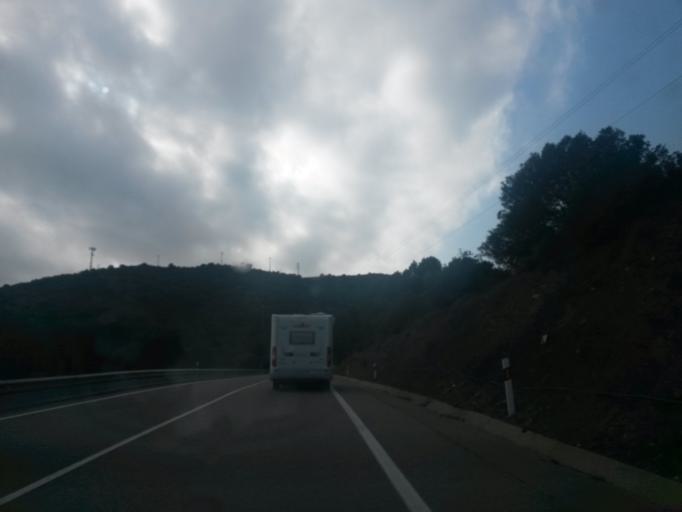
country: ES
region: Catalonia
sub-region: Provincia de Girona
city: Colera
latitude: 42.3925
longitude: 3.1521
